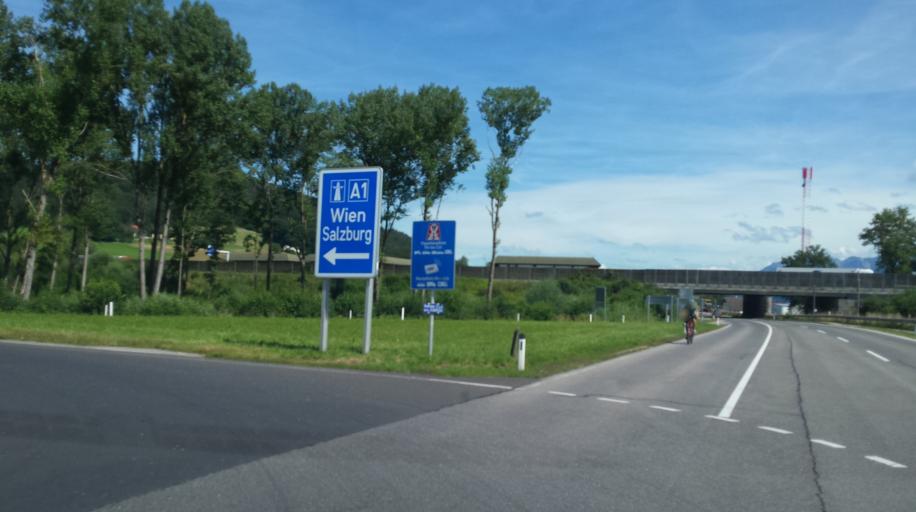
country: AT
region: Upper Austria
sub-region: Politischer Bezirk Vocklabruck
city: Sankt Georgen im Attergau
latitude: 47.9275
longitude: 13.5047
